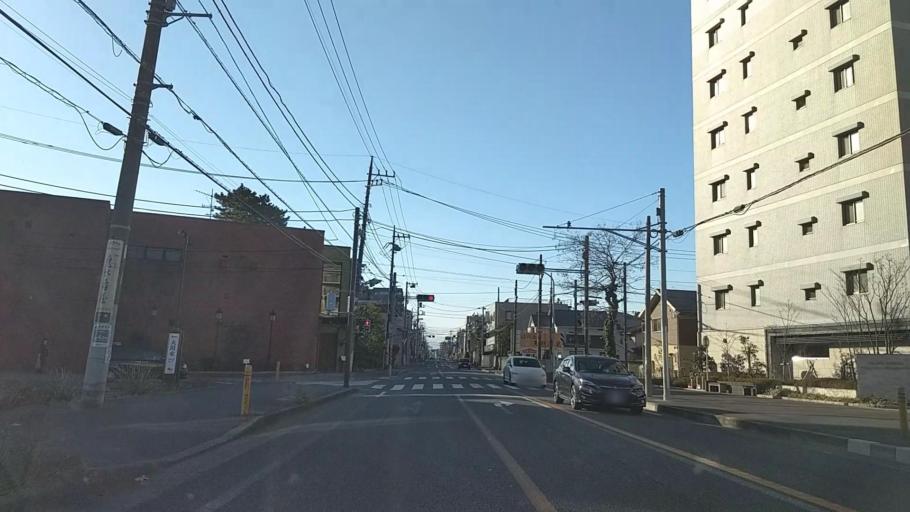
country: JP
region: Kanagawa
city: Fujisawa
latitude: 35.3287
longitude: 139.4876
